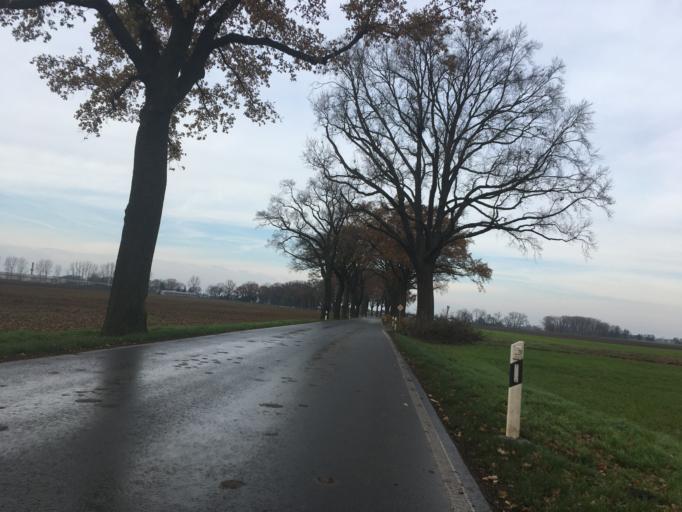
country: DE
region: Brandenburg
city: Letschin
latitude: 52.7044
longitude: 14.3851
